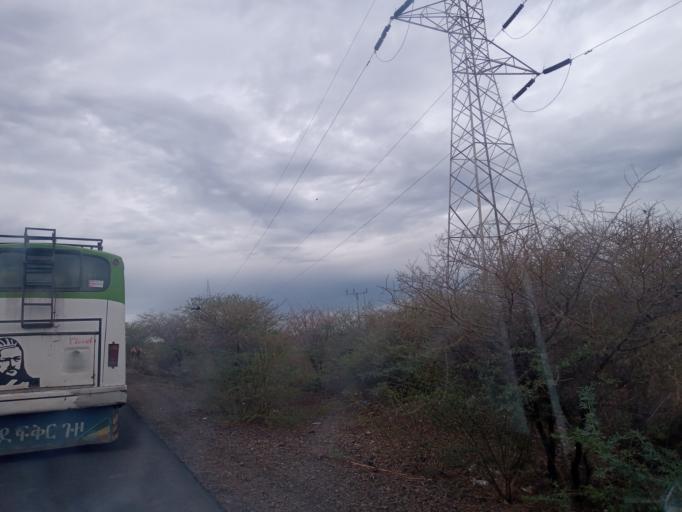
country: ET
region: Afar
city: Awash
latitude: 9.0647
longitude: 40.4176
